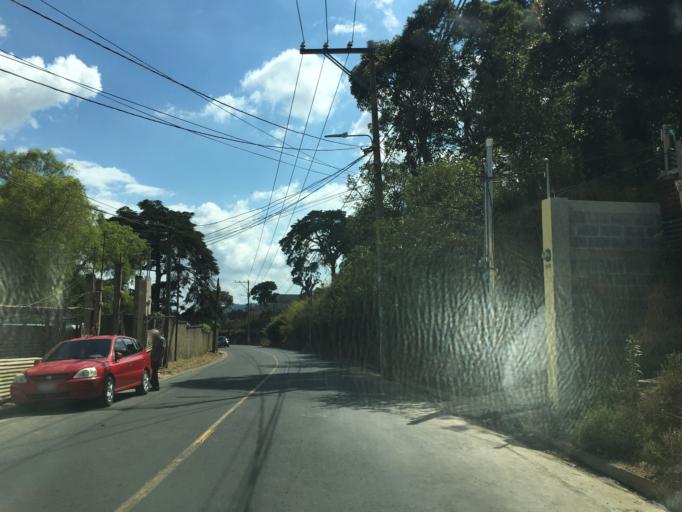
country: GT
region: Guatemala
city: San Jose Pinula
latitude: 14.5582
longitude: -90.4437
